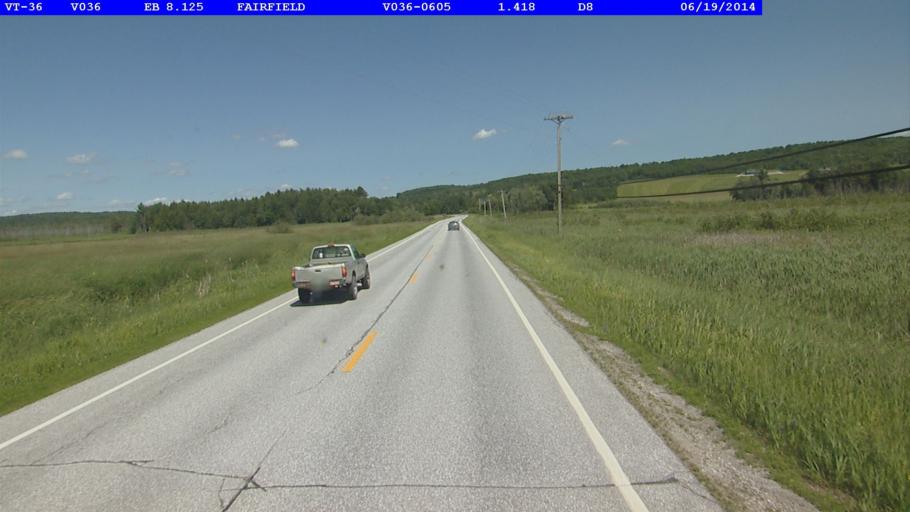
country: US
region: Vermont
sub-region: Franklin County
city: Saint Albans
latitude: 44.7873
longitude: -73.0034
